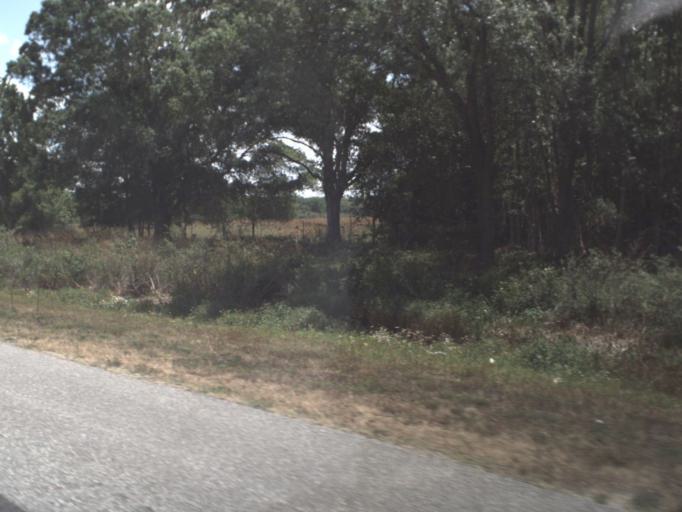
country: US
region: Florida
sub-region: Orange County
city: Wedgefield
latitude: 28.4513
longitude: -81.1166
